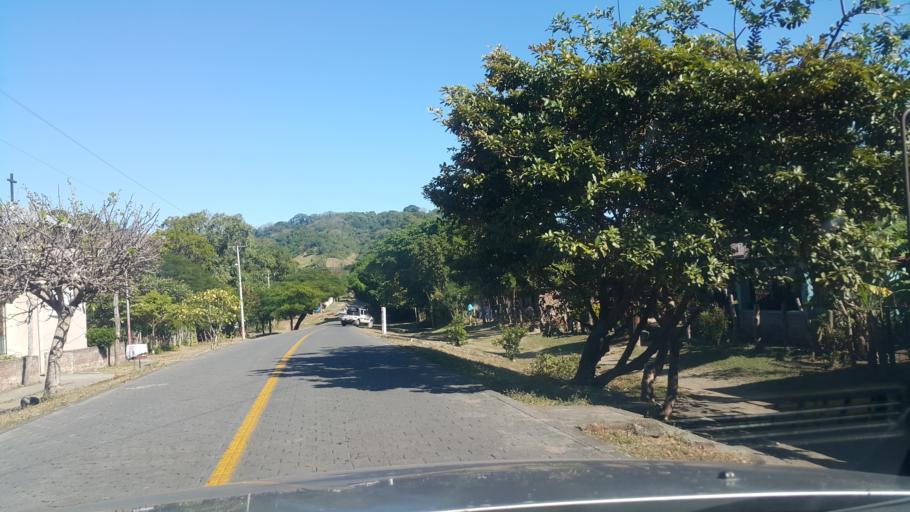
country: NI
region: Rivas
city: Moyogalpa
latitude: 11.4859
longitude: -85.6410
